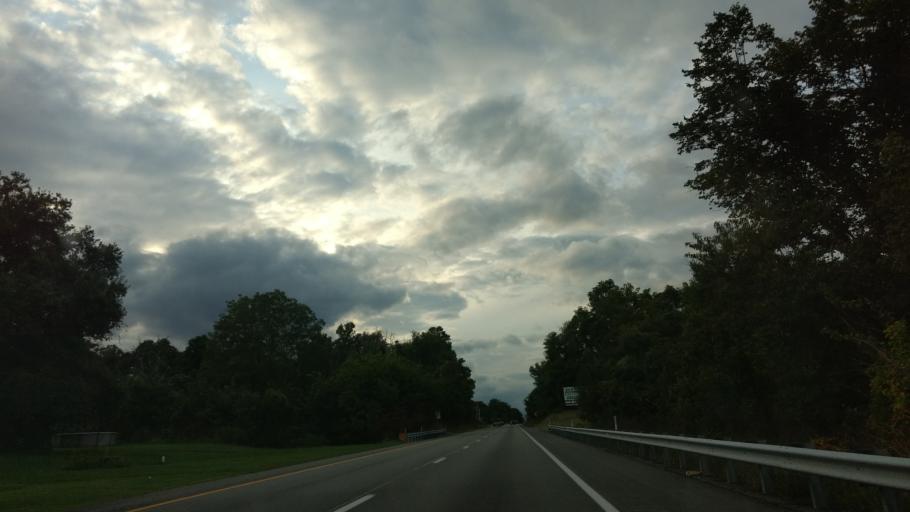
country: US
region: Pennsylvania
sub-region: Westmoreland County
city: Fellsburg
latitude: 40.1989
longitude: -79.8306
